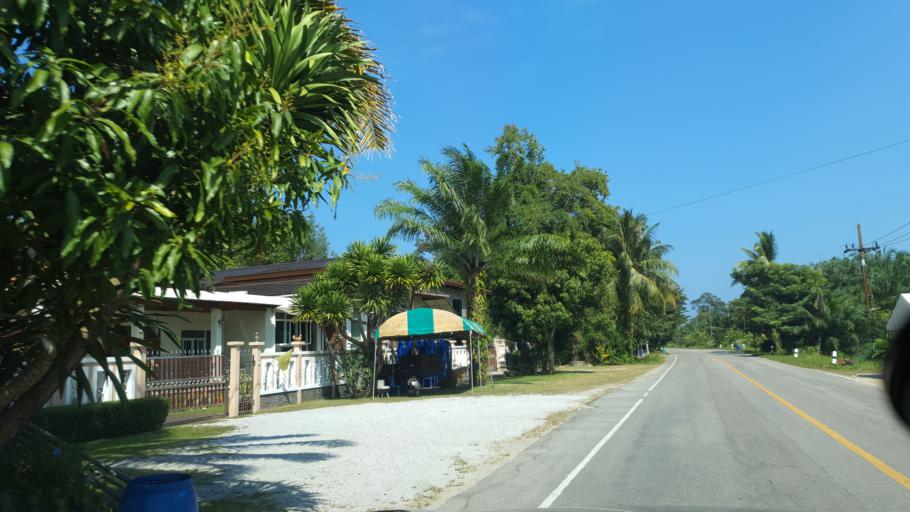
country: TH
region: Surat Thani
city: Tha Chana
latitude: 9.5772
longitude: 99.1857
